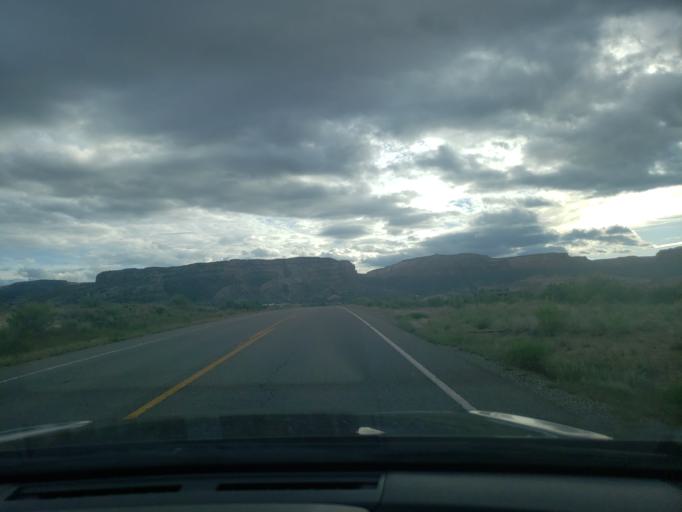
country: US
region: Colorado
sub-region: Mesa County
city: Redlands
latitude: 39.0474
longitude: -108.6154
